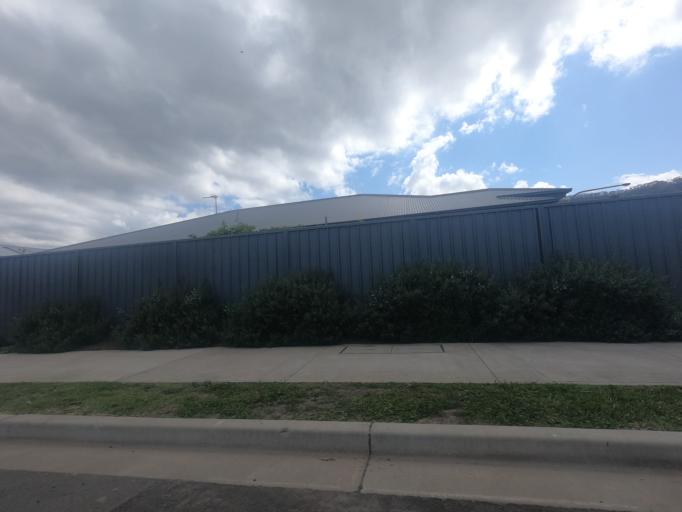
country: AU
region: New South Wales
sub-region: Wollongong
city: Dapto
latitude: -34.4752
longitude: 150.7624
